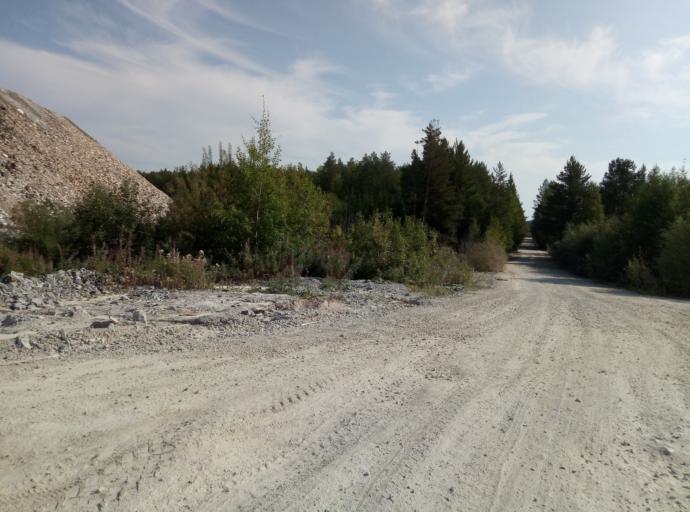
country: RU
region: Sverdlovsk
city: Rudnichnyy
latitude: 59.6589
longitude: 60.1983
